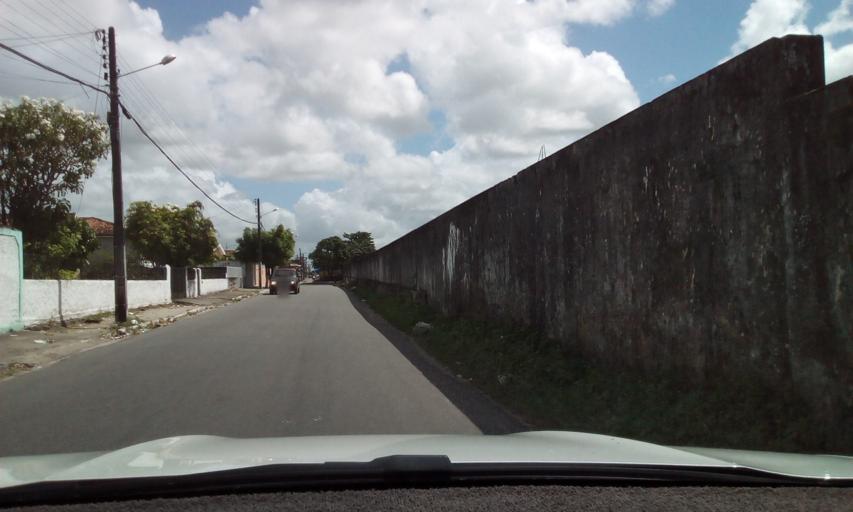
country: BR
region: Paraiba
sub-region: Bayeux
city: Bayeux
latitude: -7.1280
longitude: -34.9270
